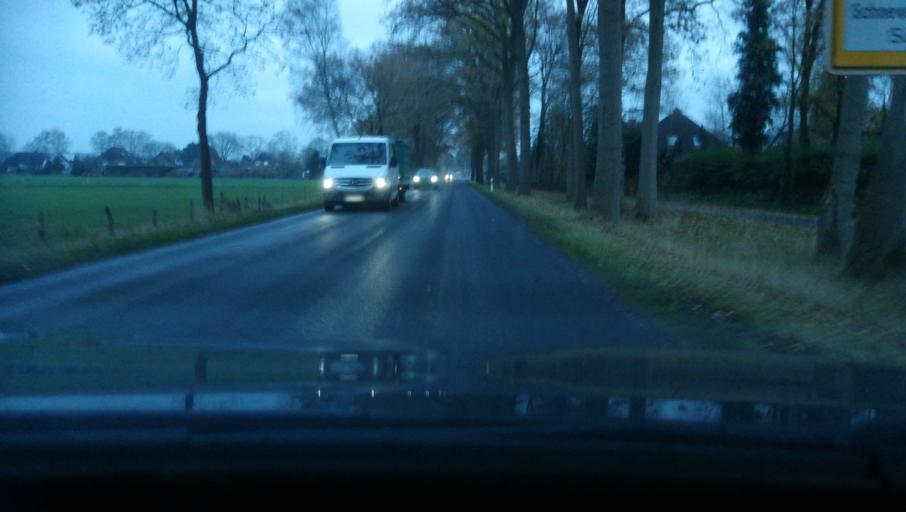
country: DE
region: Lower Saxony
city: Schneverdingen
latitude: 53.1163
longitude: 9.7619
